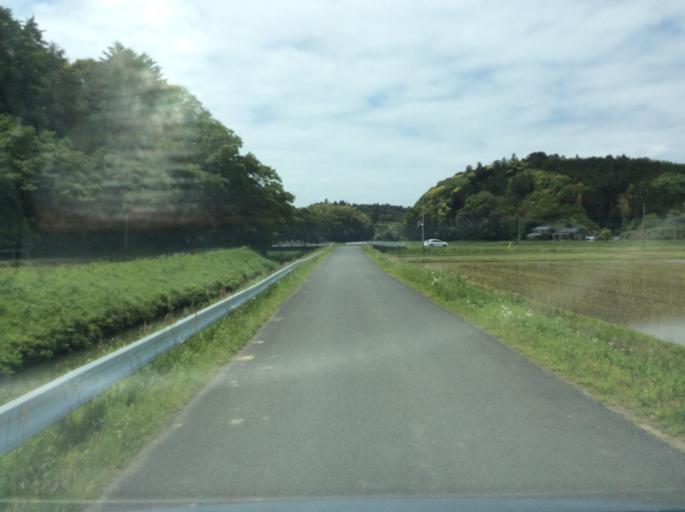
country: JP
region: Fukushima
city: Iwaki
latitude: 37.0259
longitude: 140.9390
